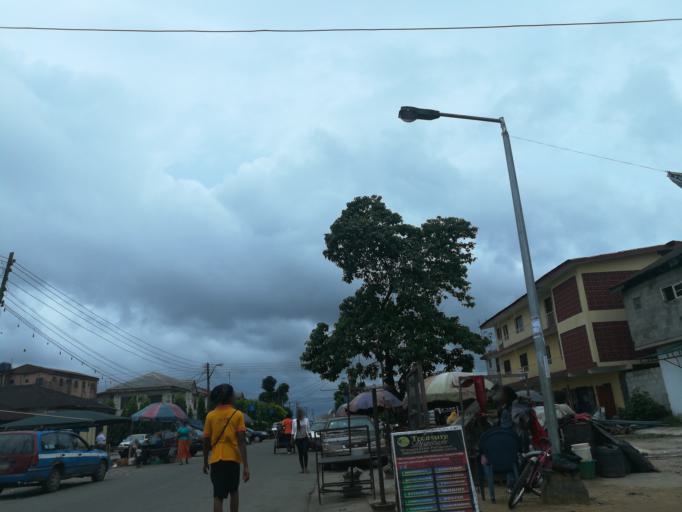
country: NG
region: Rivers
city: Port Harcourt
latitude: 4.7610
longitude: 7.0239
